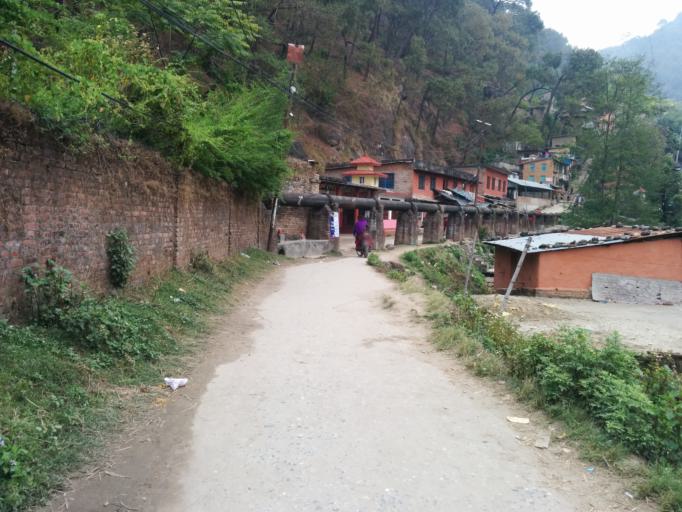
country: NP
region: Central Region
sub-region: Bagmati Zone
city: Bhaktapur
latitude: 27.7607
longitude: 85.4211
